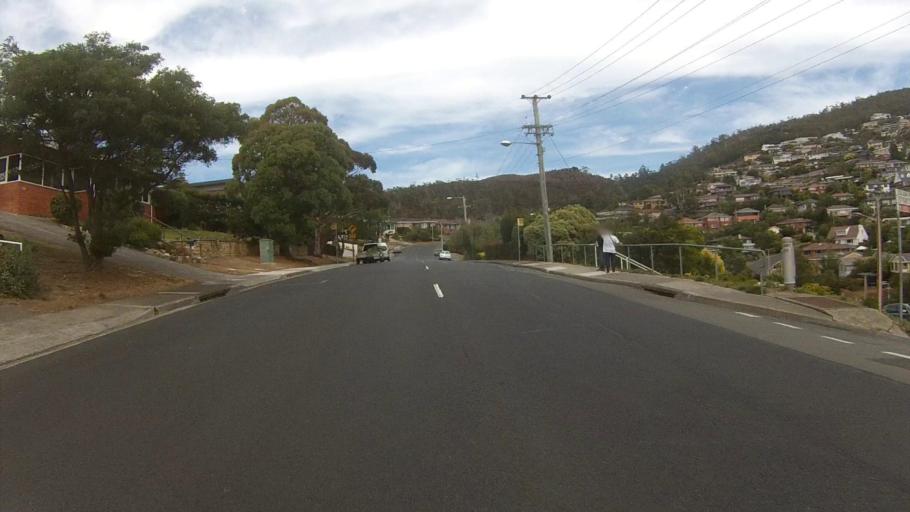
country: AU
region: Tasmania
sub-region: Kingborough
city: Taroona
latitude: -42.9171
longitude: 147.3555
